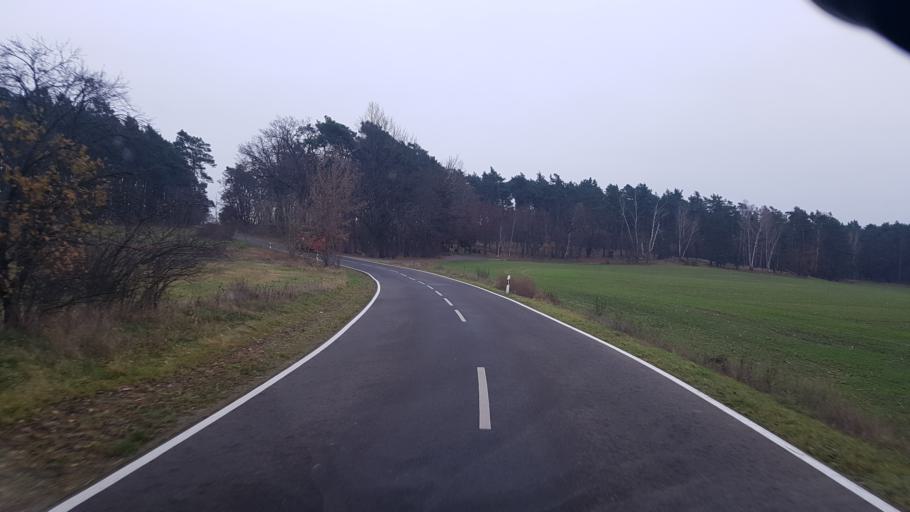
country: DE
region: Brandenburg
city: Schenkendobern
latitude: 51.9630
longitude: 14.6595
